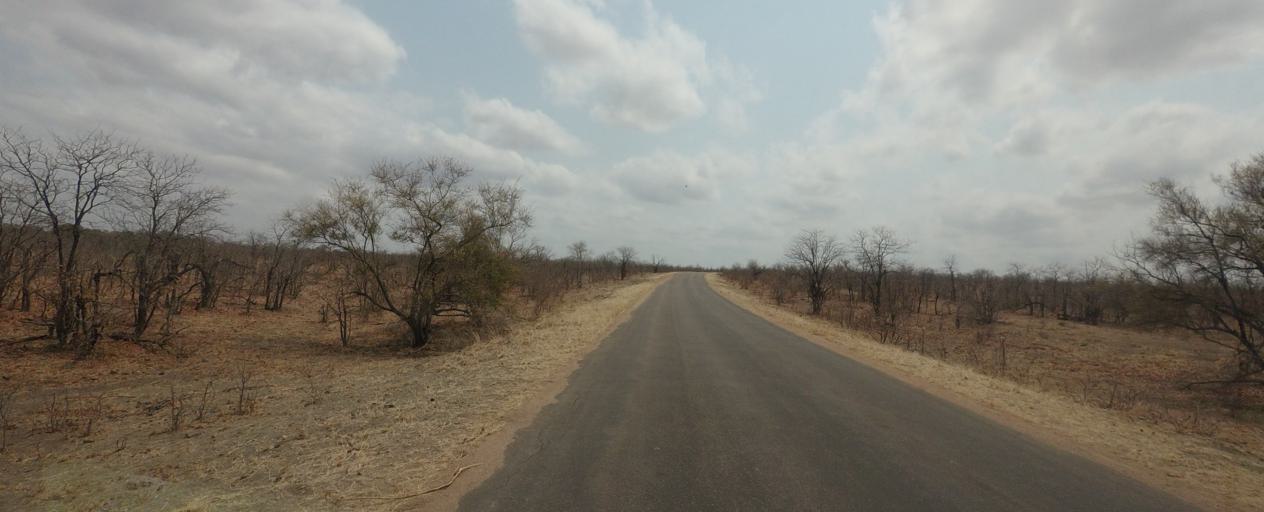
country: ZA
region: Limpopo
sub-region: Mopani District Municipality
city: Phalaborwa
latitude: -23.5859
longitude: 31.4505
